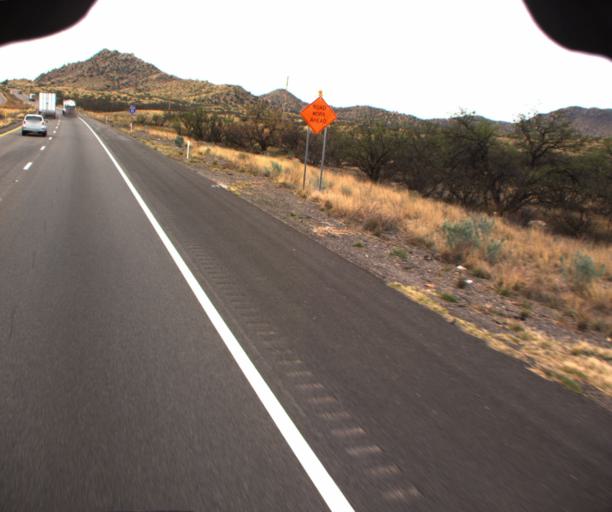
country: US
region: Arizona
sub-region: Cochise County
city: Saint David
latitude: 32.0784
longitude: -110.0584
